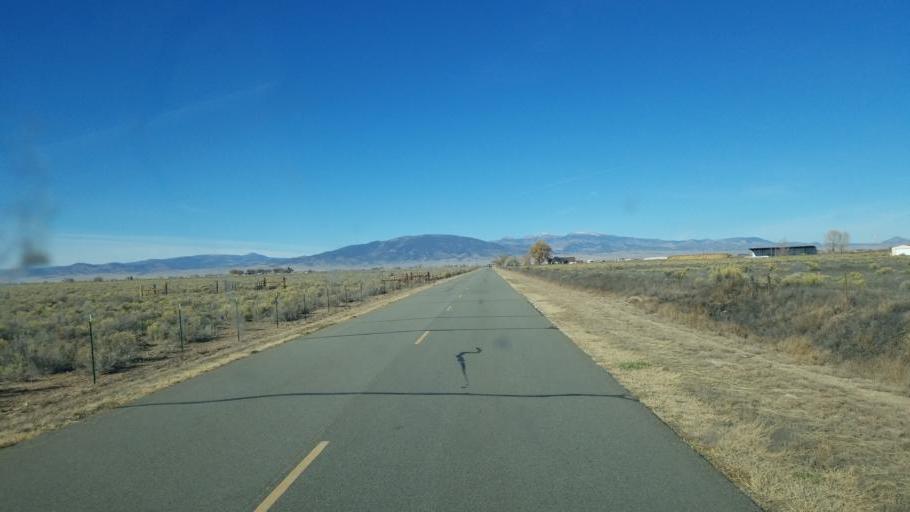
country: US
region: Colorado
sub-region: Alamosa County
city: Alamosa
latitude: 37.4587
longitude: -106.0147
